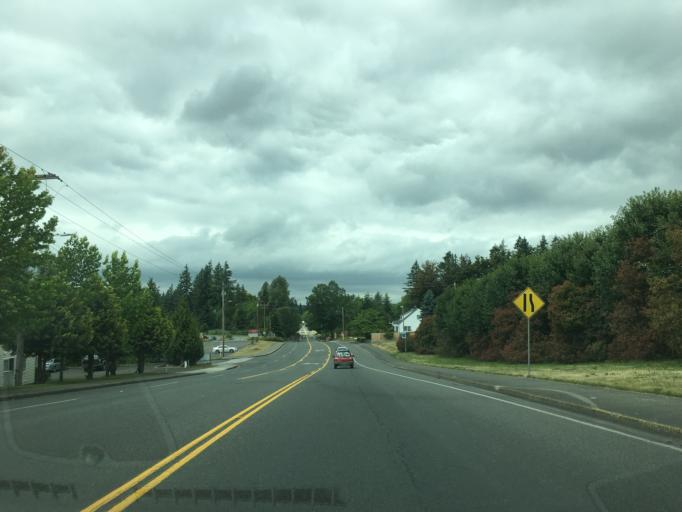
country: US
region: Washington
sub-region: Snohomish County
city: Marysville
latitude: 48.0745
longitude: -122.1408
